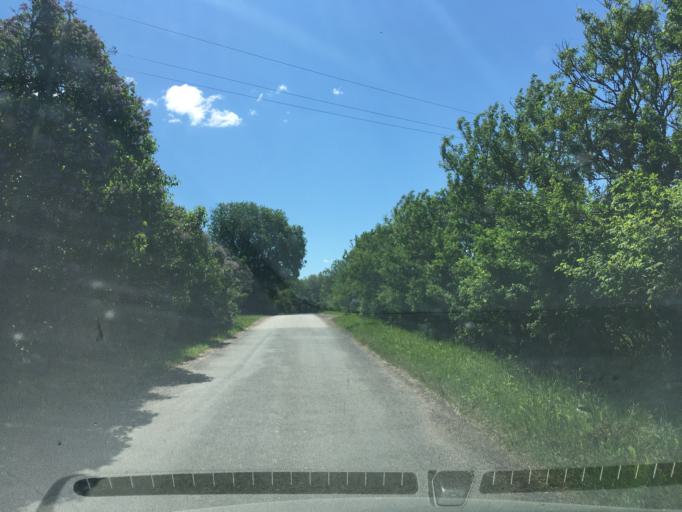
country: EE
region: Harju
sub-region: Rae vald
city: Vaida
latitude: 59.1623
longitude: 25.1253
